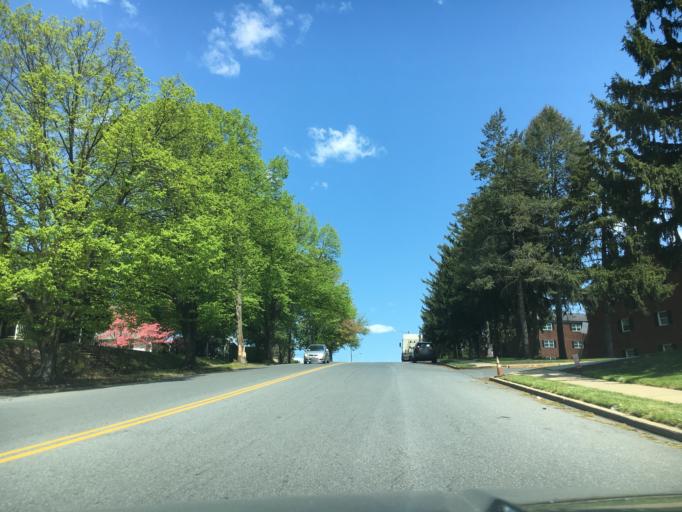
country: US
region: Pennsylvania
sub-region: Lehigh County
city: Allentown
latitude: 40.5855
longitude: -75.4789
